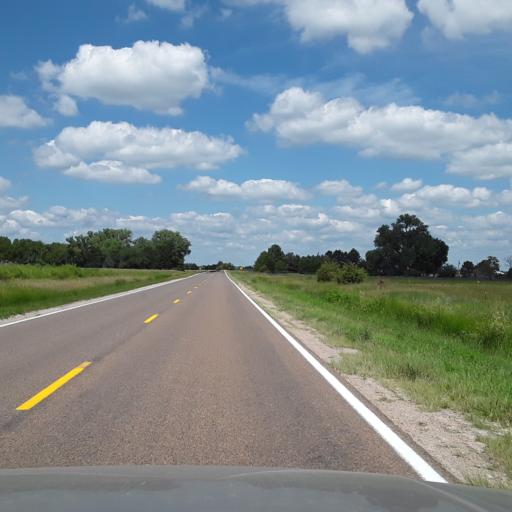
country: US
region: Nebraska
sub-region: Nance County
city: Genoa
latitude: 41.3912
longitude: -97.6942
